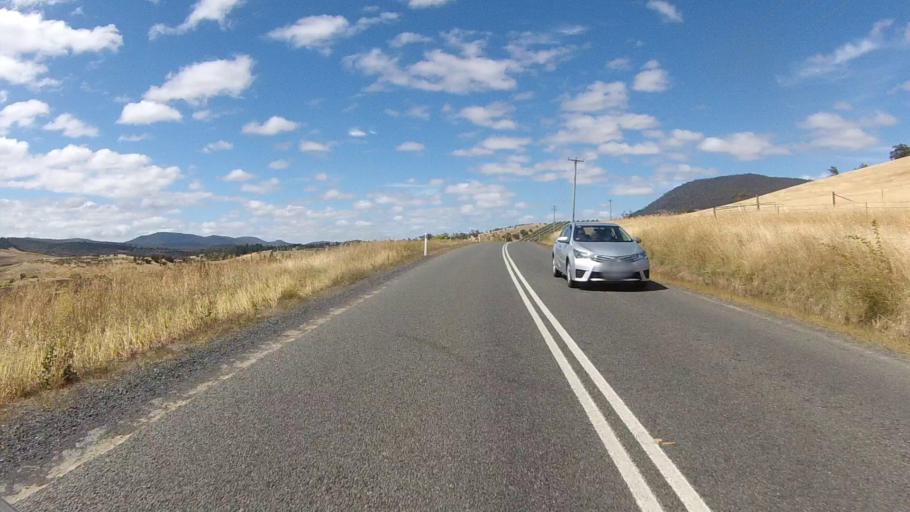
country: AU
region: Tasmania
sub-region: Brighton
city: Old Beach
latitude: -42.5988
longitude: 147.4157
